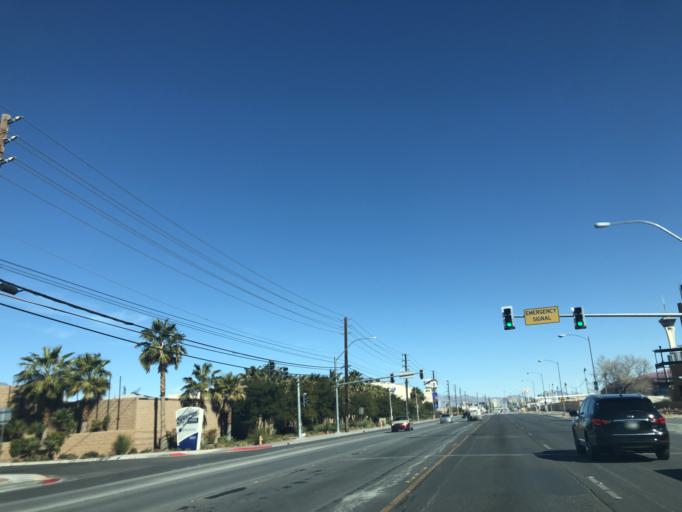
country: US
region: Nevada
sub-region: Clark County
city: Paradise
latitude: 36.1332
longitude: -115.1720
